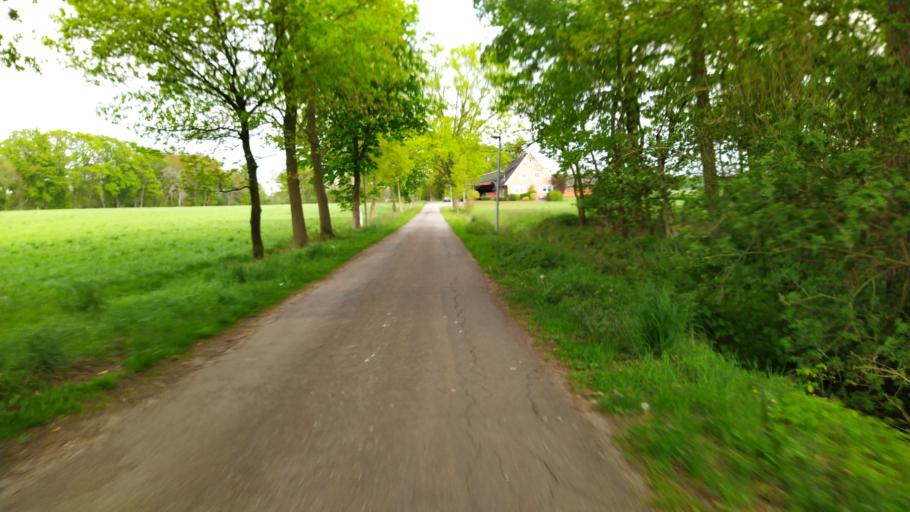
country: DE
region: Lower Saxony
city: Ahlerstedt
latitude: 53.4021
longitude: 9.4144
